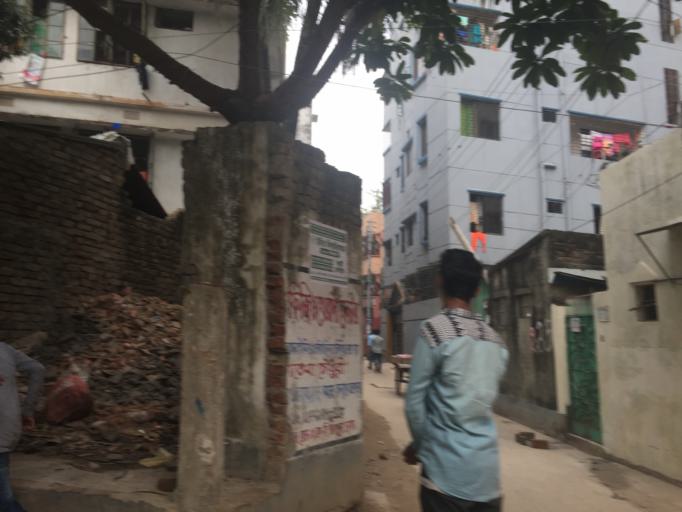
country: BD
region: Dhaka
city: Azimpur
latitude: 23.7868
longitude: 90.3618
